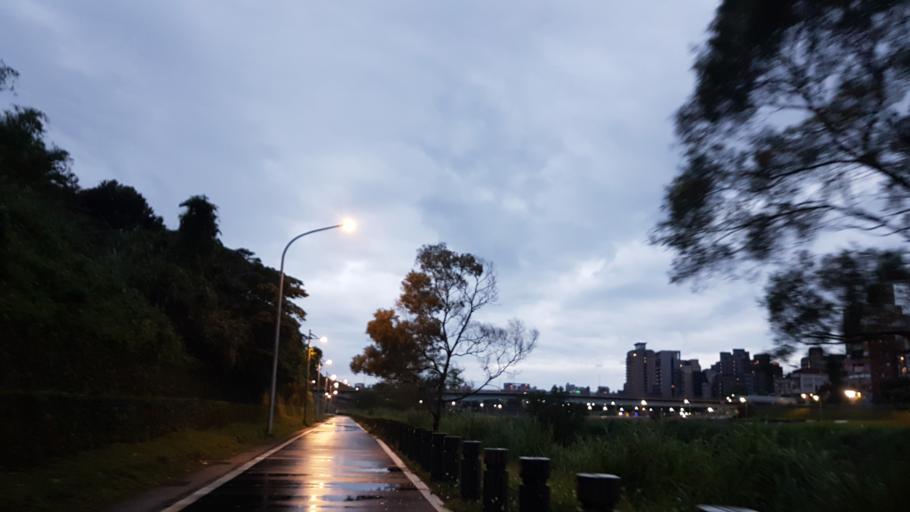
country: TW
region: Taipei
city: Taipei
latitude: 24.9812
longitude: 121.5702
